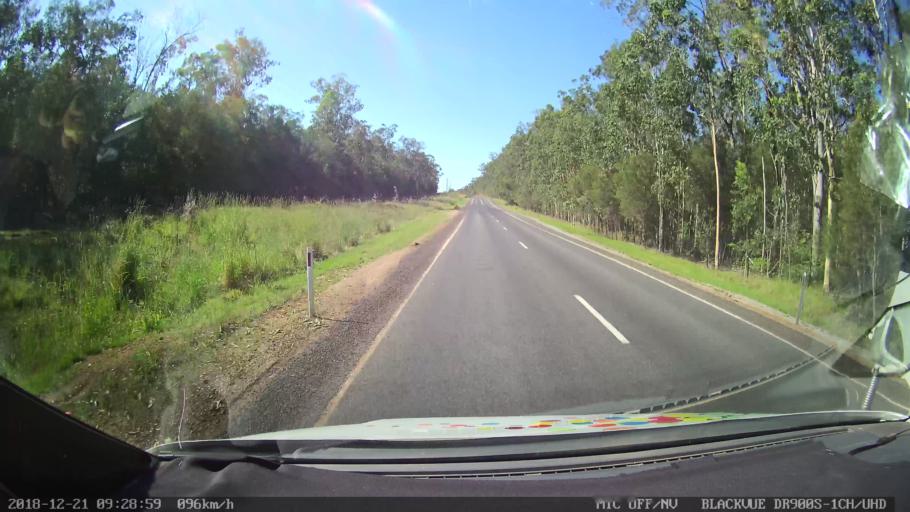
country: AU
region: New South Wales
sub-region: Clarence Valley
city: Maclean
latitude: -29.4253
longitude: 152.9886
